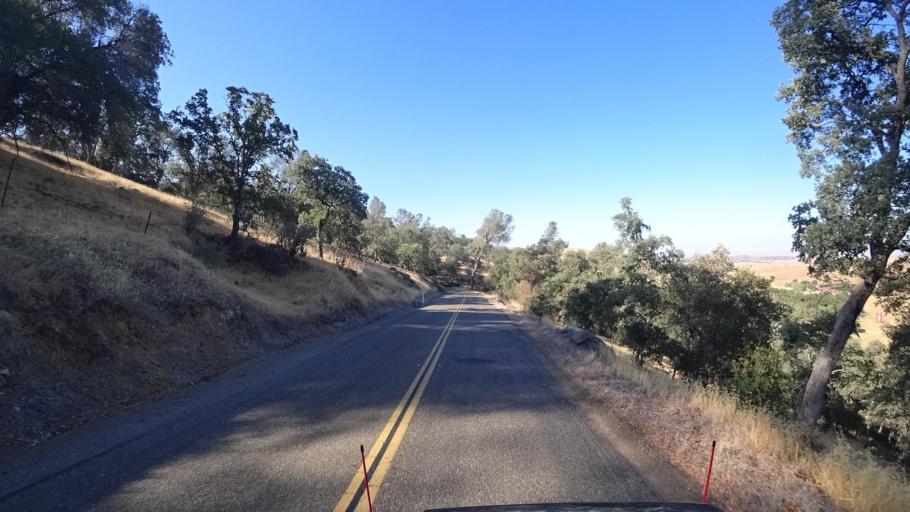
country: US
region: California
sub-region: Mariposa County
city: Mariposa
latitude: 37.5545
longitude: -120.1743
